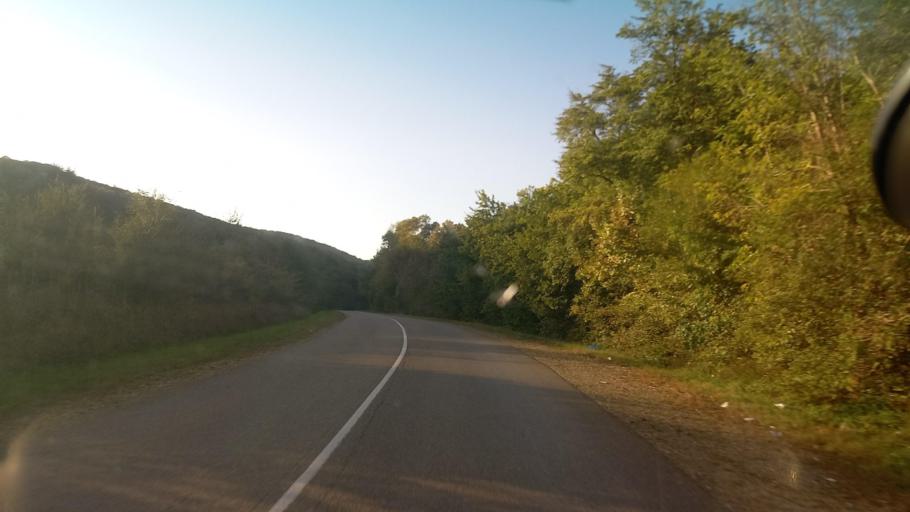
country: RU
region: Krasnodarskiy
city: Krymsk
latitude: 44.8831
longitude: 37.9030
